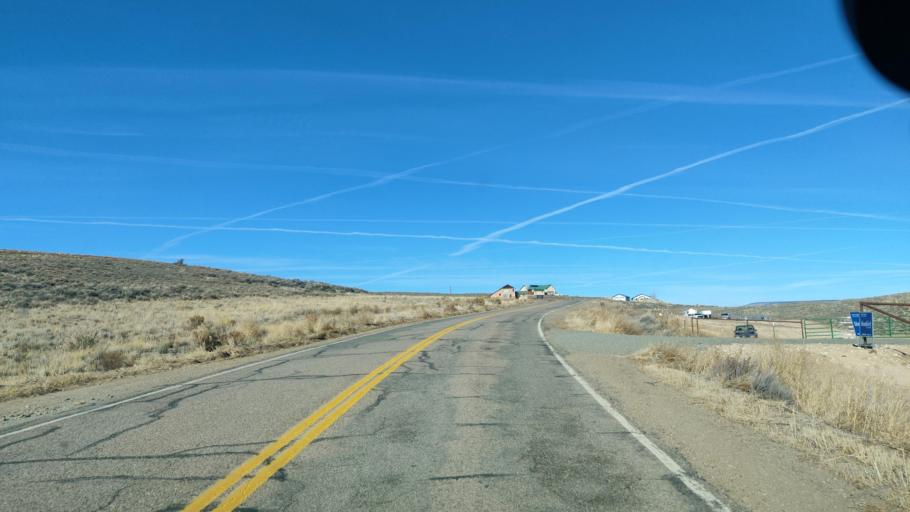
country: US
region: Colorado
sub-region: Gunnison County
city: Gunnison
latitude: 38.5377
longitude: -106.9584
